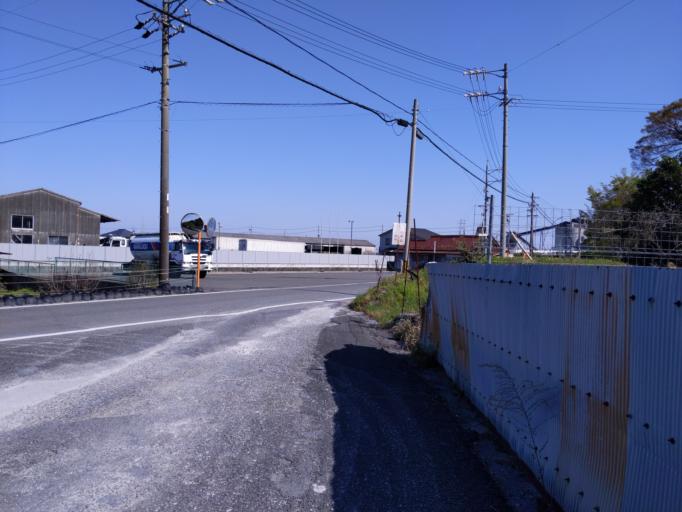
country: JP
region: Gifu
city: Godo
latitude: 35.4072
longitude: 136.5784
